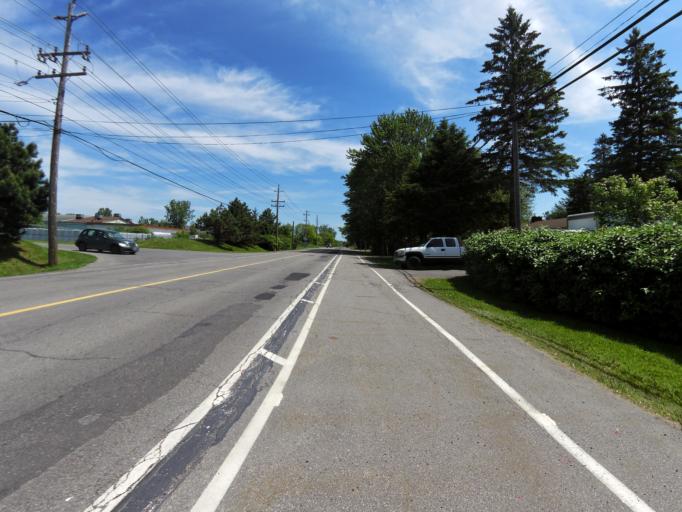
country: CA
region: Ontario
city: Ottawa
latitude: 45.3247
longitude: -75.7158
